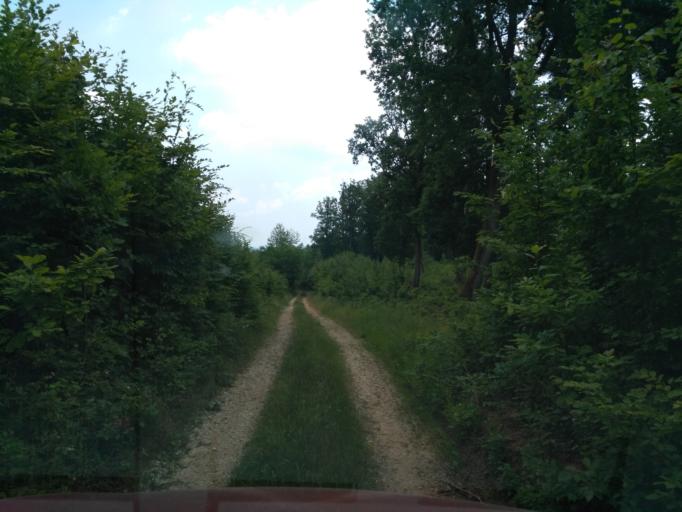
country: SK
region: Kosicky
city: Moldava nad Bodvou
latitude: 48.6556
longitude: 21.0448
